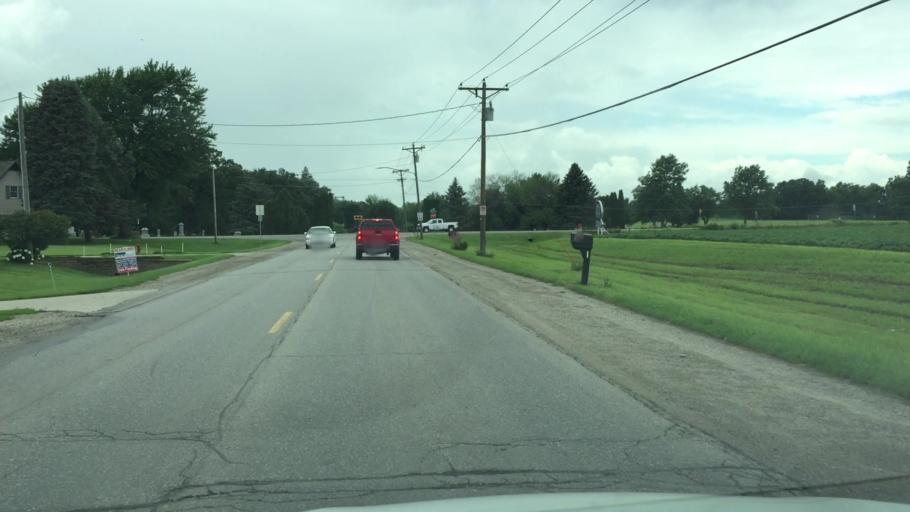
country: US
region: Iowa
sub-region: Jasper County
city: Newton
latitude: 41.7172
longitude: -93.0564
